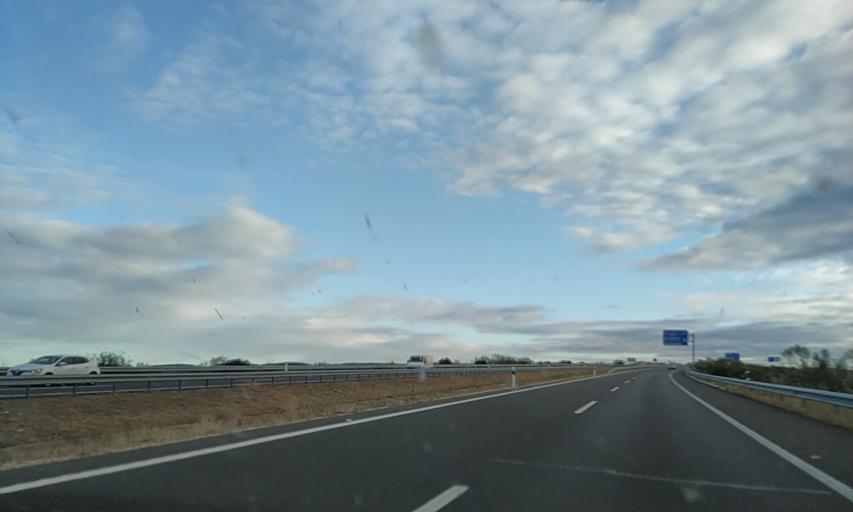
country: ES
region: Extremadura
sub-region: Provincia de Caceres
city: Casar de Caceres
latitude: 39.5251
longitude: -6.4176
